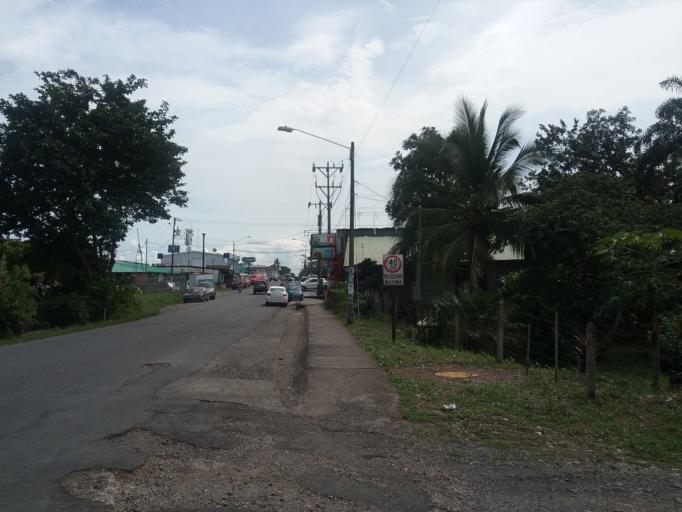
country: CR
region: Limon
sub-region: Canton de Pococi
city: Guapiles
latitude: 10.3204
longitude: -83.8889
